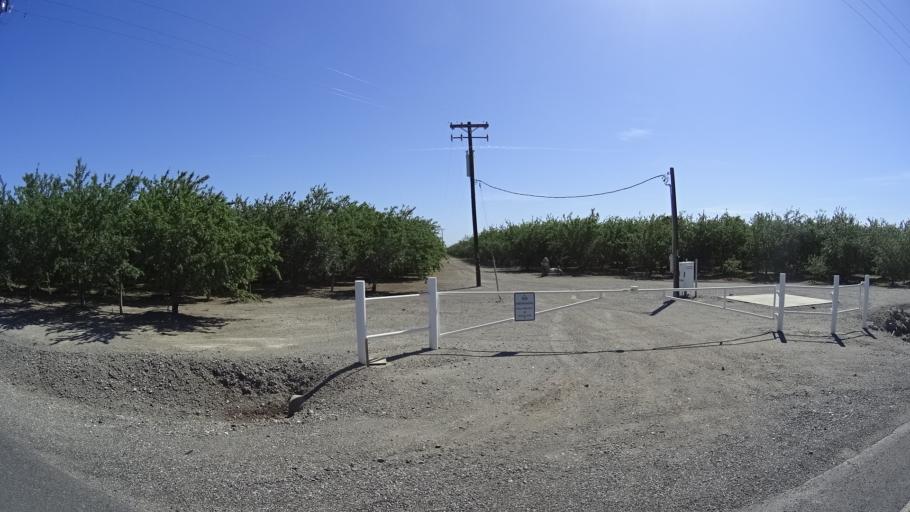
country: US
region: California
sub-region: Glenn County
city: Hamilton City
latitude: 39.7139
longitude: -122.1043
